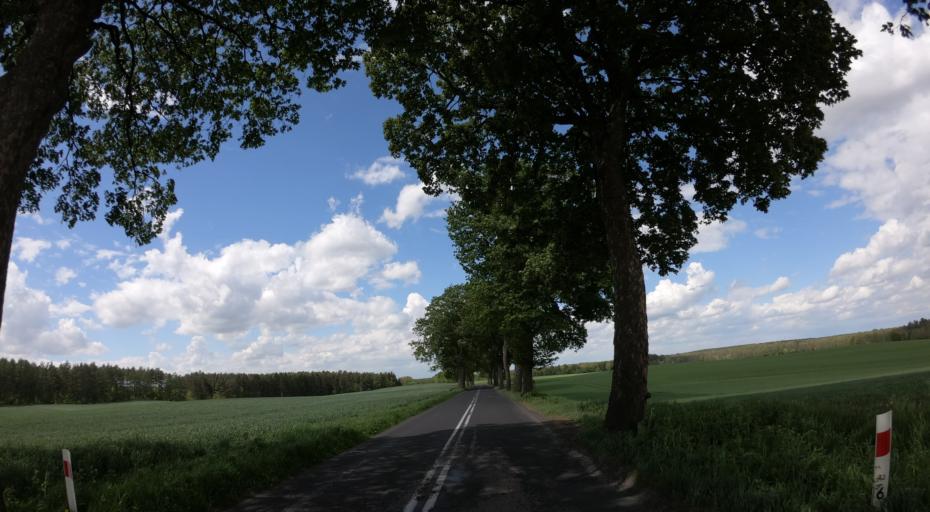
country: PL
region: West Pomeranian Voivodeship
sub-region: Powiat lobeski
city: Lobez
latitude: 53.5982
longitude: 15.7151
